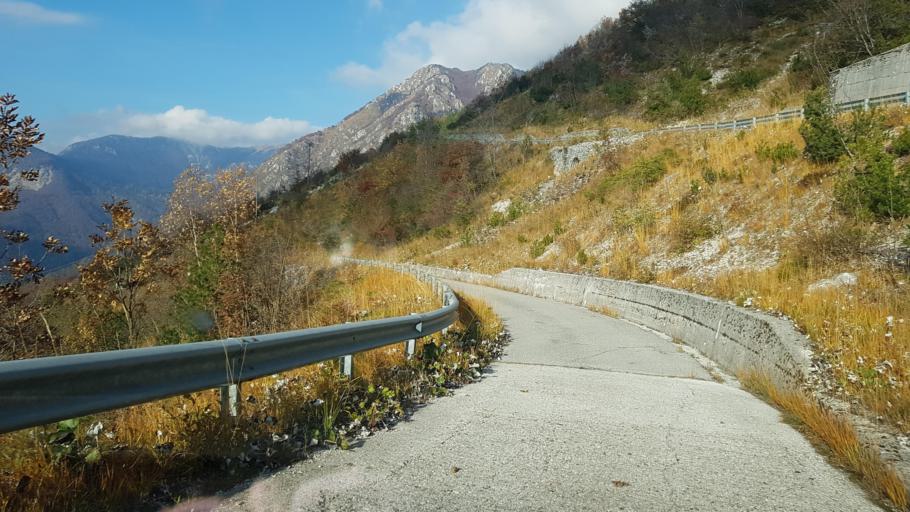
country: IT
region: Friuli Venezia Giulia
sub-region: Provincia di Udine
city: Moggio Udinese
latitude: 46.4547
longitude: 13.2063
